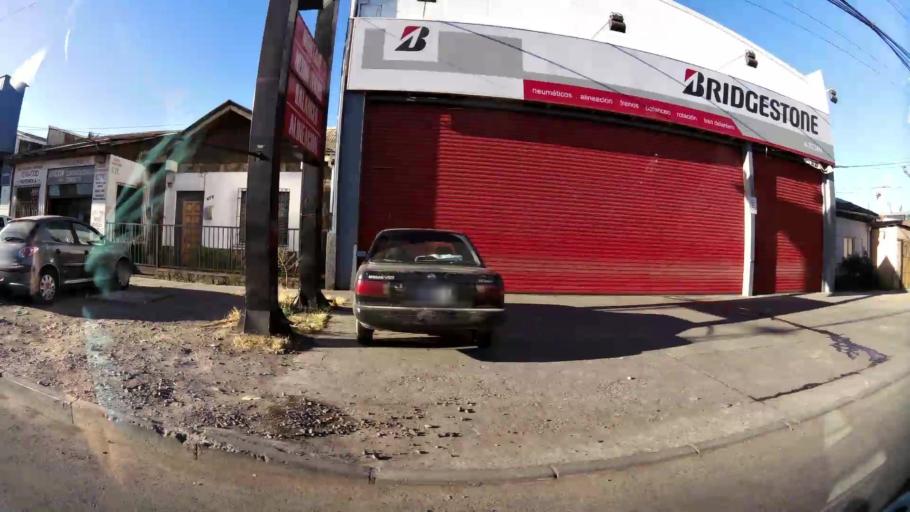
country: CL
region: Maule
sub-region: Provincia de Curico
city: Curico
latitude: -34.9767
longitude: -71.2423
